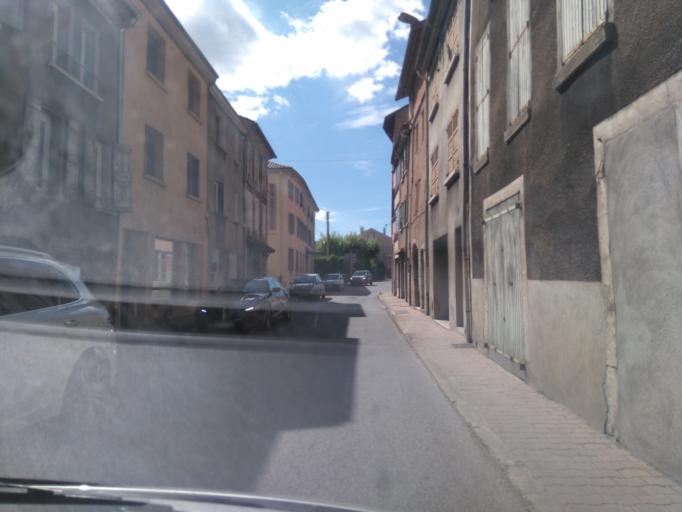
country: FR
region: Provence-Alpes-Cote d'Azur
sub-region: Departement des Hautes-Alpes
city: Laragne-Monteglin
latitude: 44.3142
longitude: 5.8216
